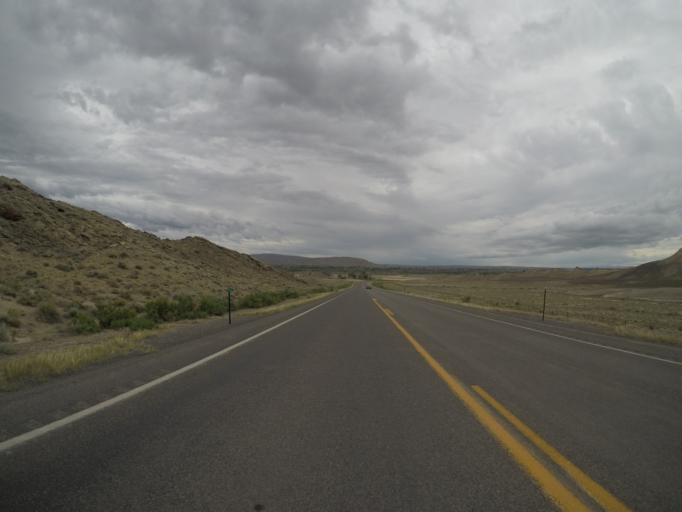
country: US
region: Wyoming
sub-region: Big Horn County
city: Lovell
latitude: 44.8841
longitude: -108.2891
